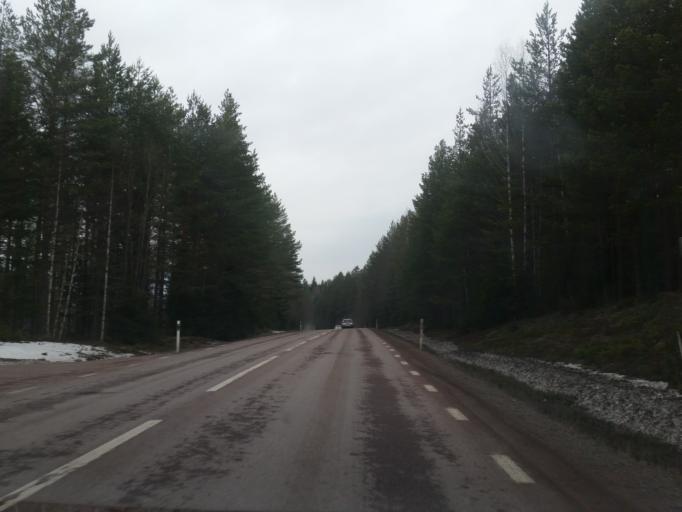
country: SE
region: Dalarna
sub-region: Mora Kommun
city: Mora
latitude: 61.0813
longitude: 14.3310
